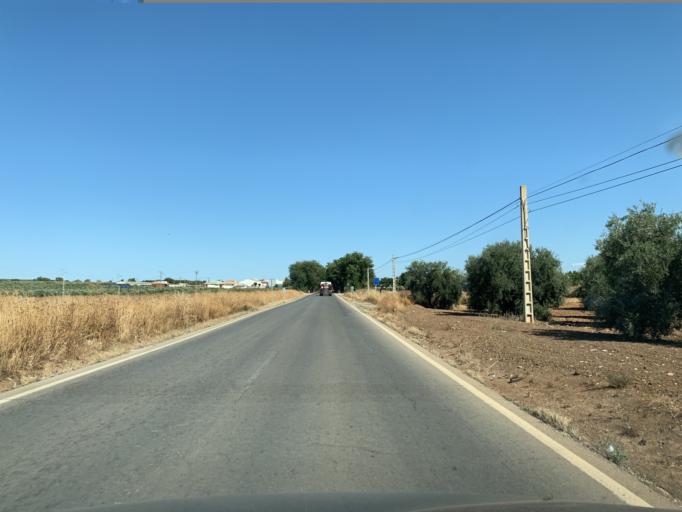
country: ES
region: Andalusia
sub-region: Provincia de Sevilla
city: Marinaleda
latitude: 37.3662
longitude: -4.9694
